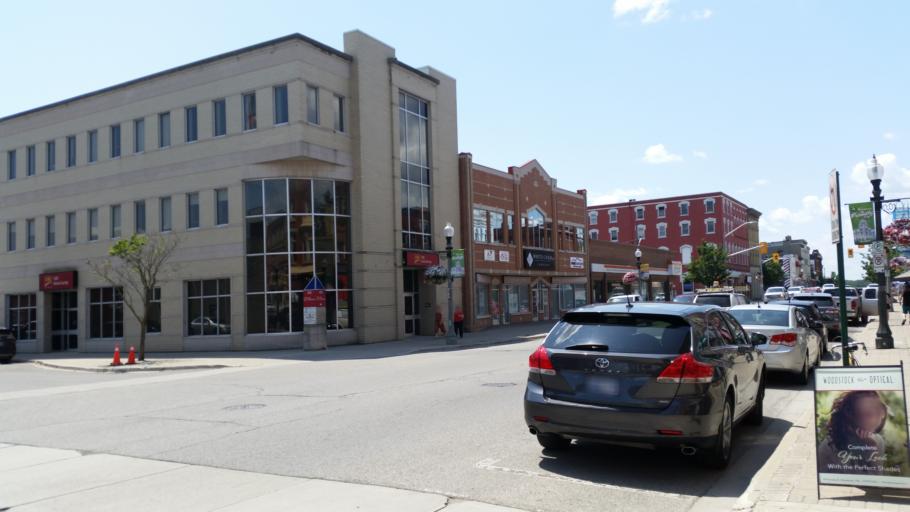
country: CA
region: Ontario
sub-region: Oxford County
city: Woodstock
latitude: 43.1299
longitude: -80.7591
